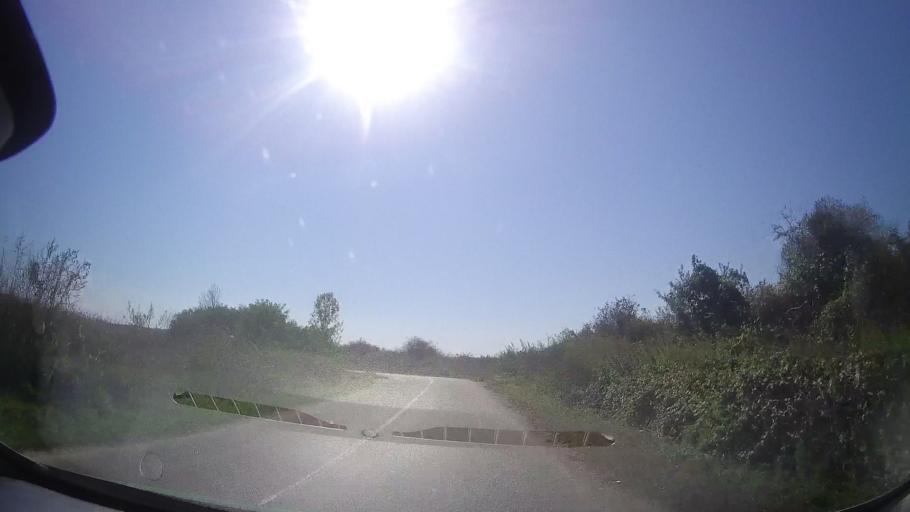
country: RO
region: Timis
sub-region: Comuna Bethausen
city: Bethausen
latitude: 45.8118
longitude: 21.9588
